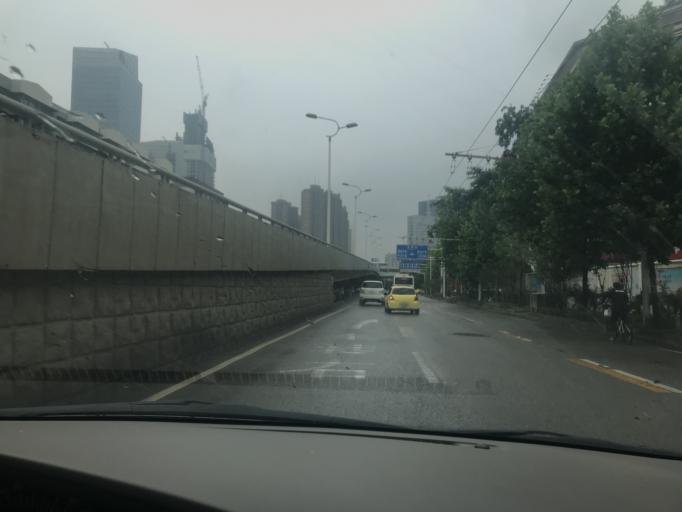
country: CN
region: Hubei
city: Jiang'an
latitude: 30.6177
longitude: 114.3063
